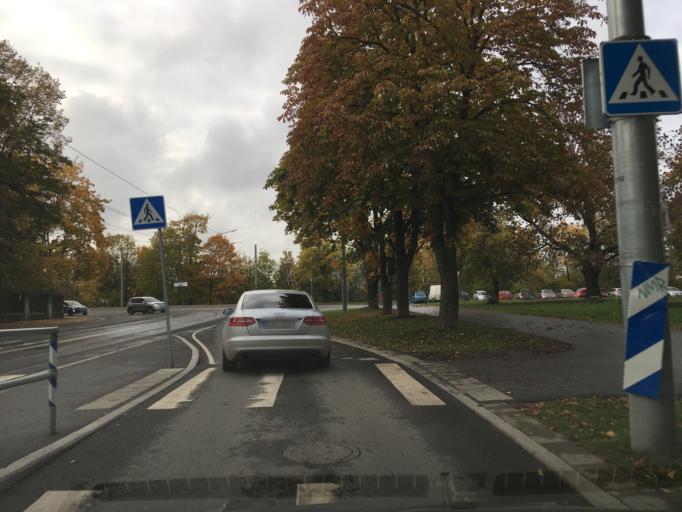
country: EE
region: Harju
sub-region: Tallinna linn
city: Tallinn
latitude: 59.4301
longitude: 24.7864
